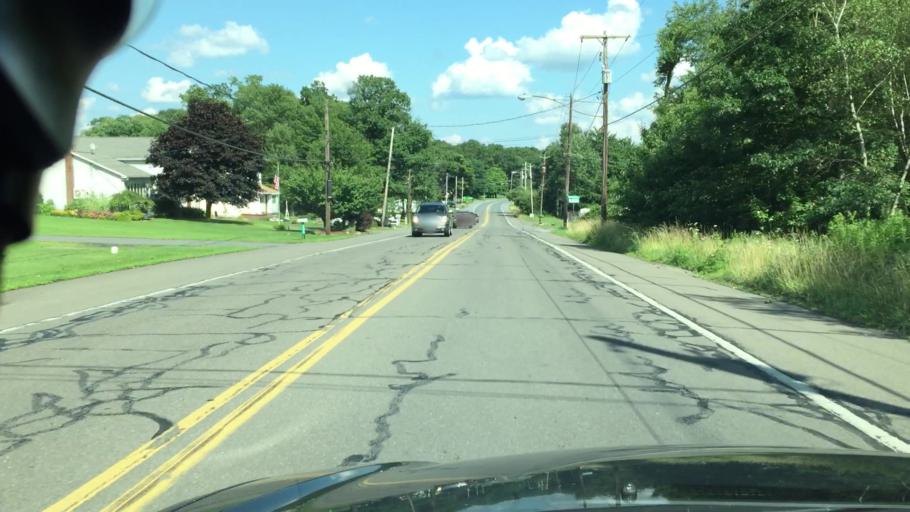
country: US
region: Pennsylvania
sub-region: Luzerne County
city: Hazleton
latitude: 40.9378
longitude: -75.9331
